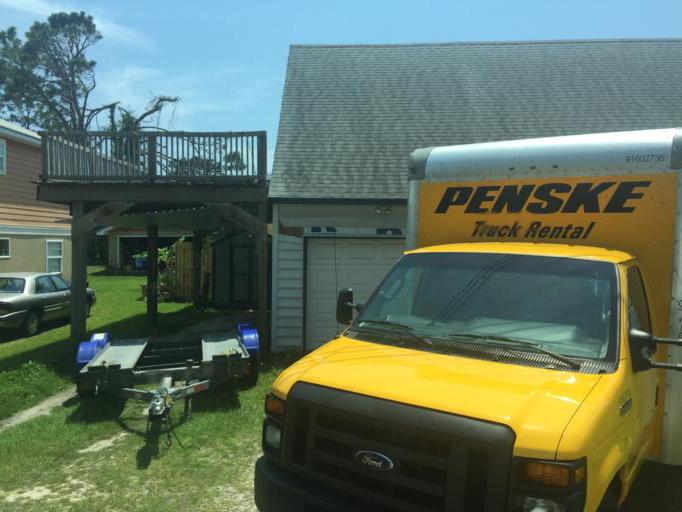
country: US
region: Florida
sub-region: Bay County
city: Lower Grand Lagoon
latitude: 30.1488
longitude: -85.7568
